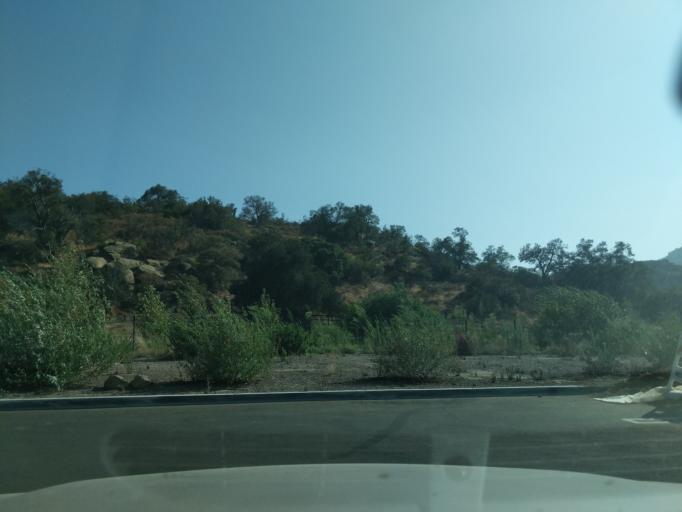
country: US
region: California
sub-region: Los Angeles County
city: Chatsworth
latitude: 34.2604
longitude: -118.6179
